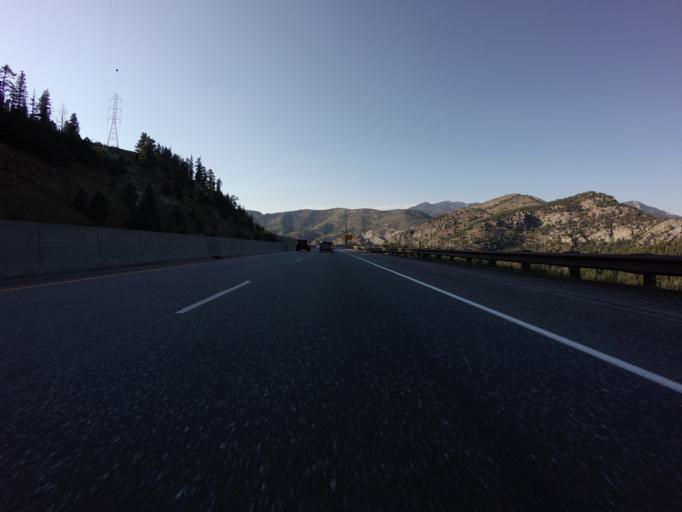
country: US
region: Colorado
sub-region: Clear Creek County
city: Idaho Springs
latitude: 39.7314
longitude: -105.4267
